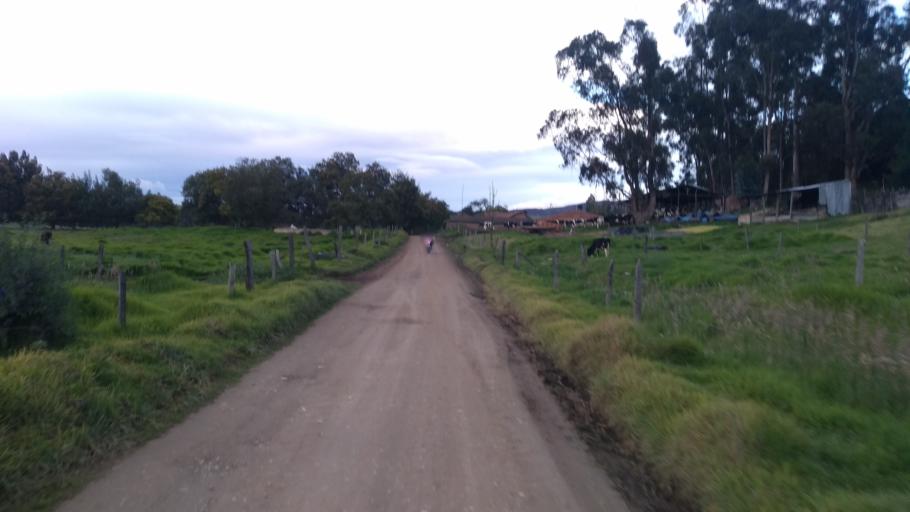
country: CO
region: Boyaca
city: Toca
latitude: 5.6204
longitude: -73.1638
